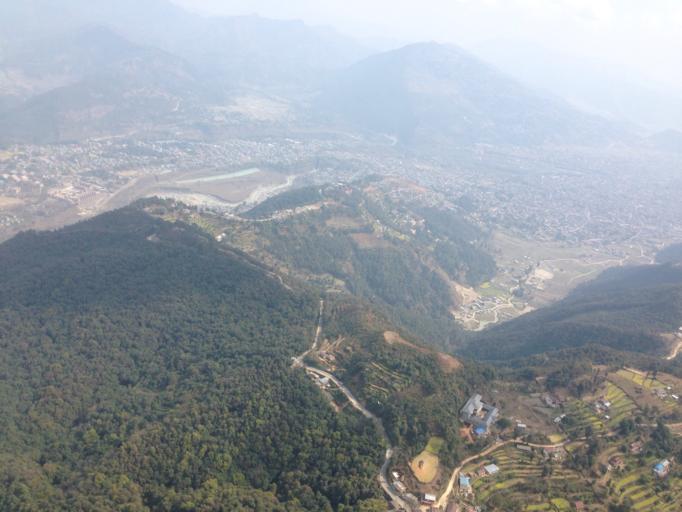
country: NP
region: Western Region
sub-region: Gandaki Zone
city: Pokhara
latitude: 28.2450
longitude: 83.9561
